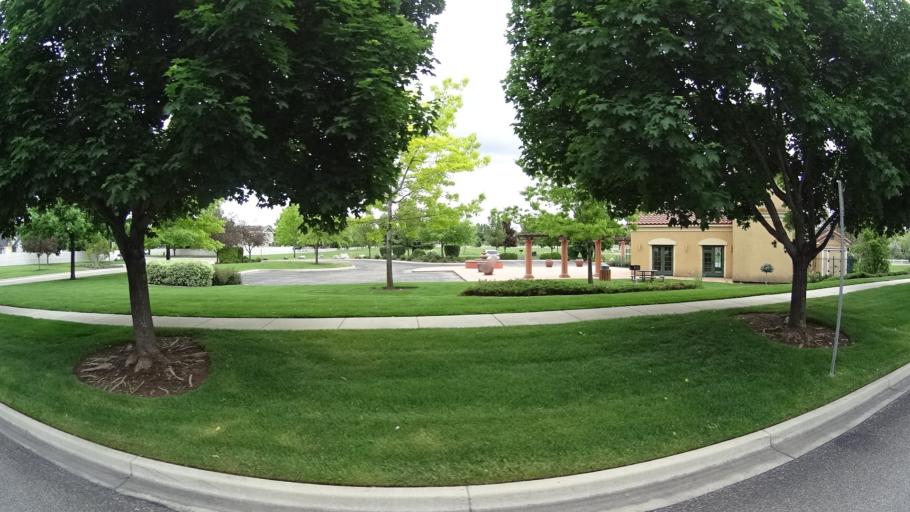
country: US
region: Idaho
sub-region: Ada County
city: Meridian
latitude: 43.6355
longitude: -116.4245
